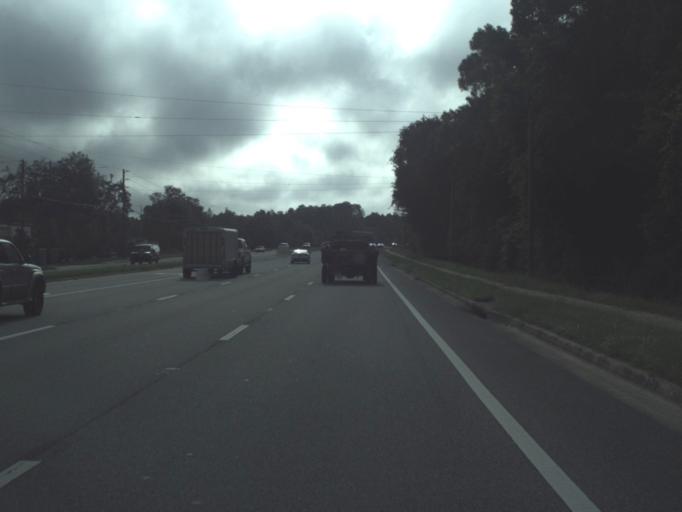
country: US
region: Florida
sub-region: Pasco County
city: Bayonet Point
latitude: 28.3320
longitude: -82.5976
